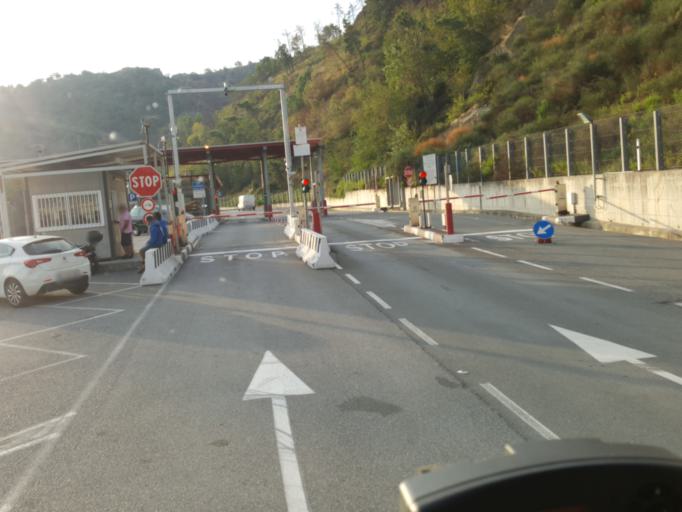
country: IT
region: Liguria
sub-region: Provincia di Savona
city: Vado Ligure
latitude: 44.2624
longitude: 8.4425
